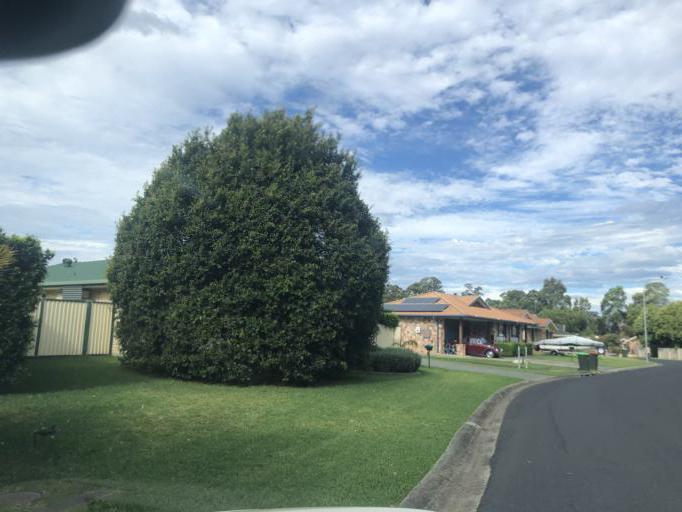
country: AU
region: New South Wales
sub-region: Coffs Harbour
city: Coffs Harbour
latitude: -30.2884
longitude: 153.0988
